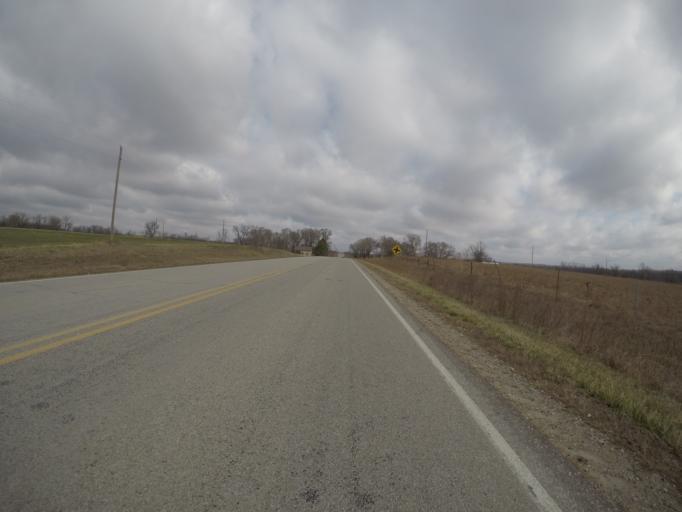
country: US
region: Kansas
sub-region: Pottawatomie County
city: Westmoreland
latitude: 39.3180
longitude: -96.4361
